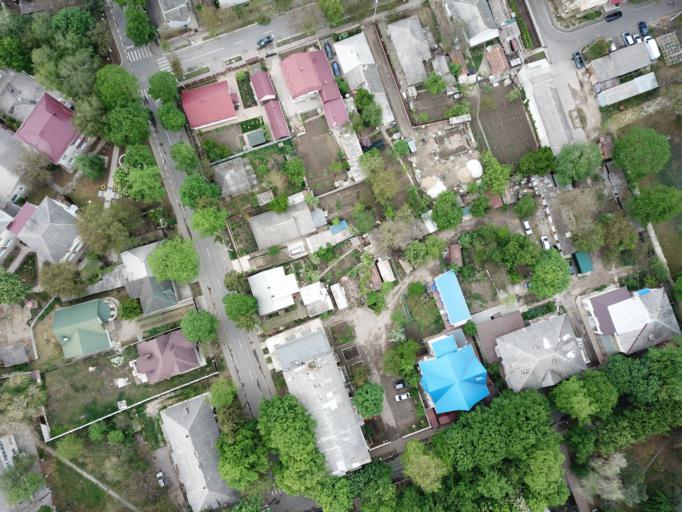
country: MD
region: Ungheni
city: Ungheni
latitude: 47.2067
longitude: 27.7975
